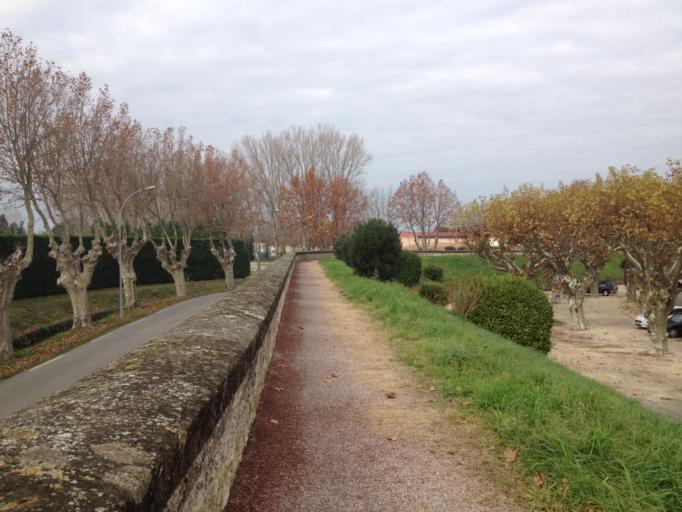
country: FR
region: Provence-Alpes-Cote d'Azur
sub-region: Departement du Vaucluse
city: Caderousse
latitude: 44.1010
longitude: 4.7543
